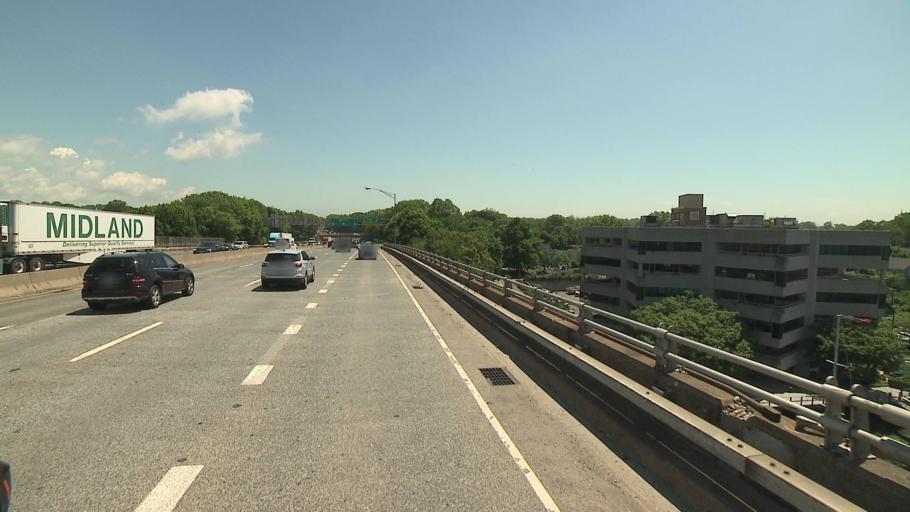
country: US
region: Connecticut
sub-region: Fairfield County
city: Norwalk
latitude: 41.1075
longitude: -73.4103
